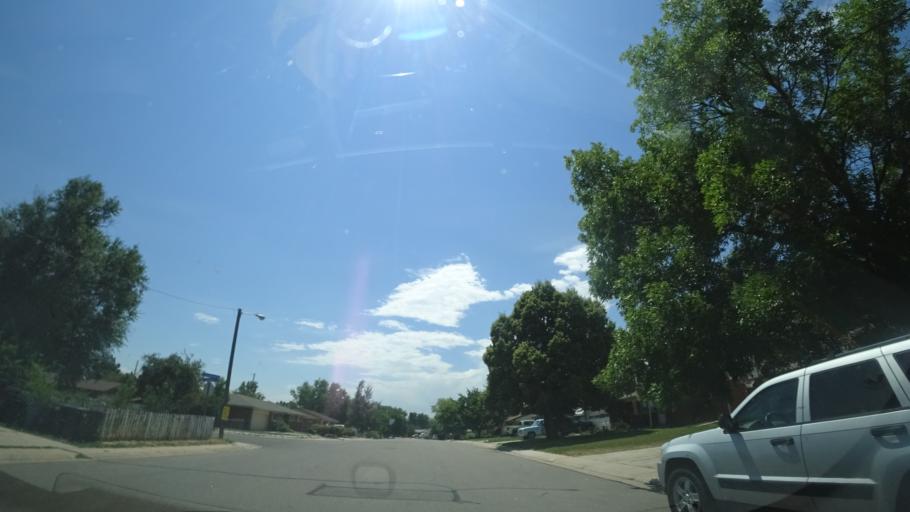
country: US
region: Colorado
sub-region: Jefferson County
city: Lakewood
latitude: 39.6925
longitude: -105.0897
